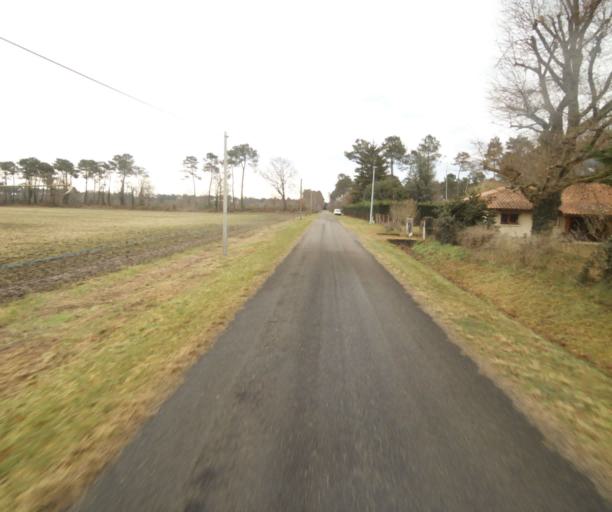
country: FR
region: Midi-Pyrenees
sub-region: Departement du Gers
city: Cazaubon
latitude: 44.0213
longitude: -0.0767
